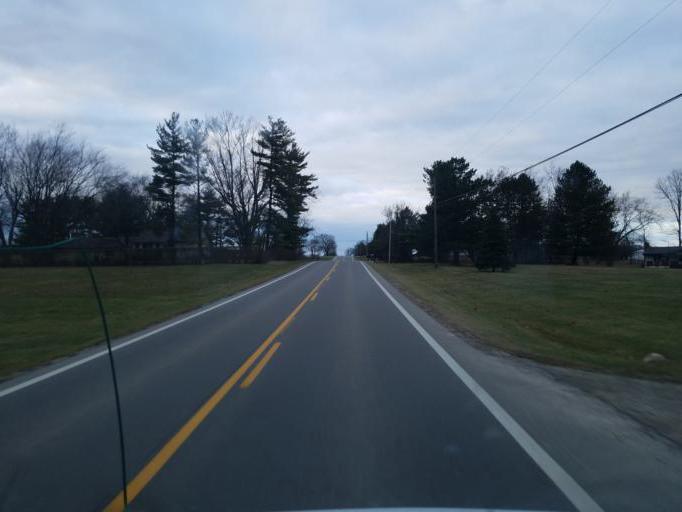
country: US
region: Ohio
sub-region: Delaware County
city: Delaware
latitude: 40.3278
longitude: -83.1301
